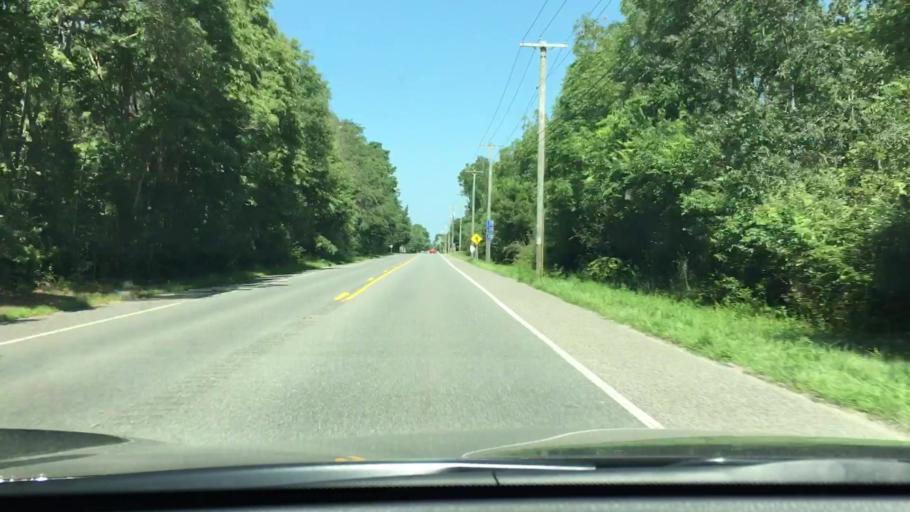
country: US
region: New Jersey
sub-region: Cumberland County
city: Laurel Lake
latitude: 39.3128
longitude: -75.0090
